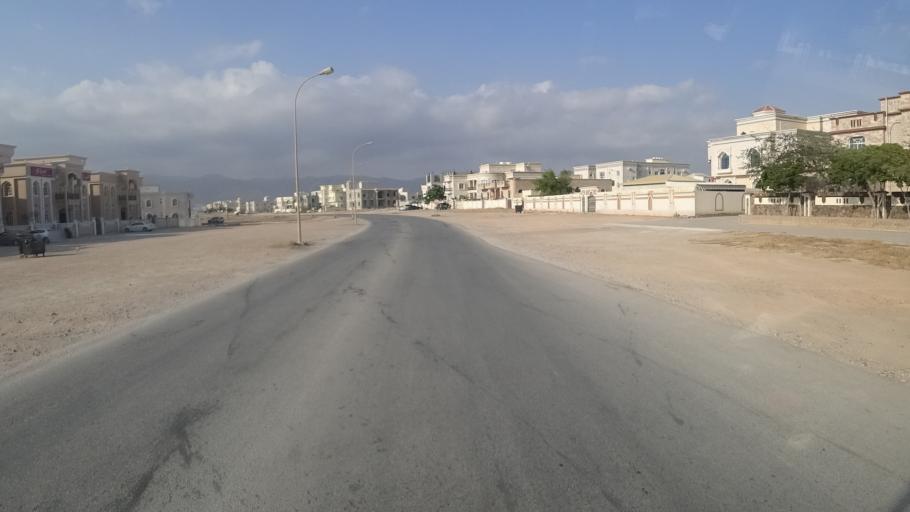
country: OM
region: Zufar
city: Salalah
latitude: 17.0081
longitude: 54.0267
